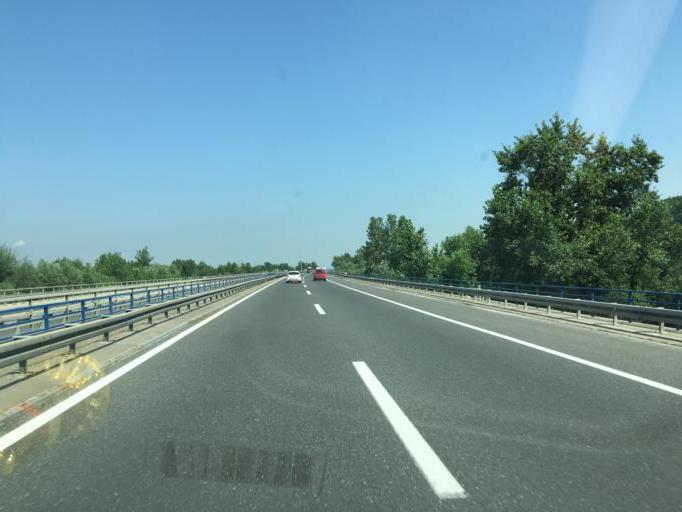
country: HR
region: Zagrebacka
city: Bestovje
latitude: 45.8273
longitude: 15.8197
